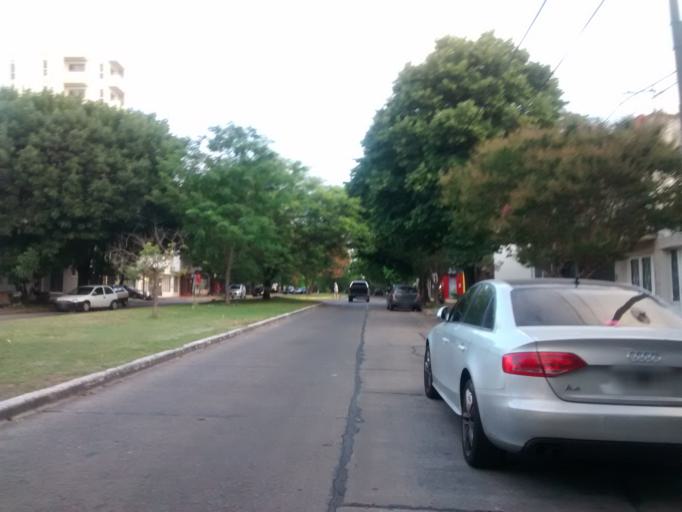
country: AR
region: Buenos Aires
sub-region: Partido de La Plata
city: La Plata
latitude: -34.9386
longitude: -57.9454
